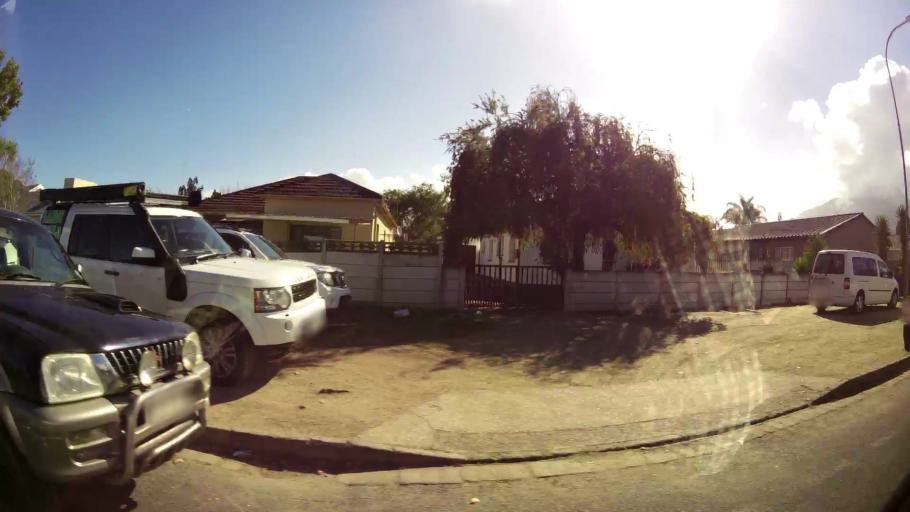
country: ZA
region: Western Cape
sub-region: Eden District Municipality
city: George
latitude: -33.9677
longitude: 22.4540
